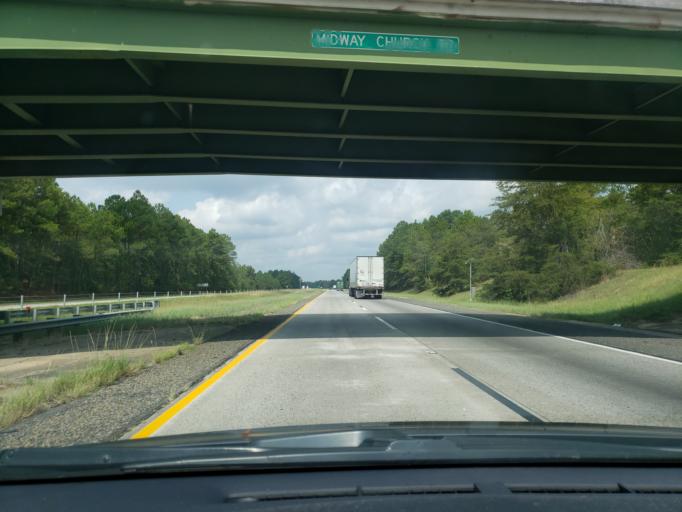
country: US
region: Georgia
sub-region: Treutlen County
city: Soperton
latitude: 32.4326
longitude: -82.5892
